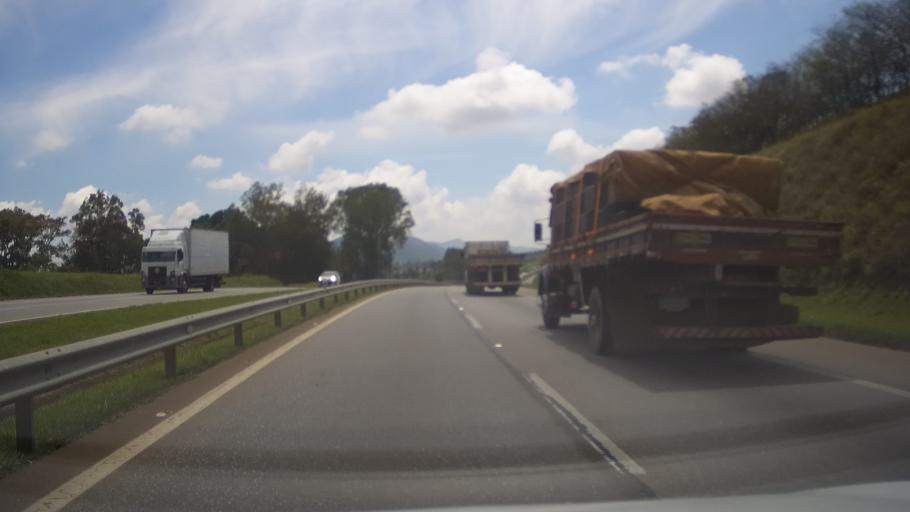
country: BR
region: Minas Gerais
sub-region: Santa Rita Do Sapucai
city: Santa Rita do Sapucai
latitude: -22.0994
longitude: -45.7202
